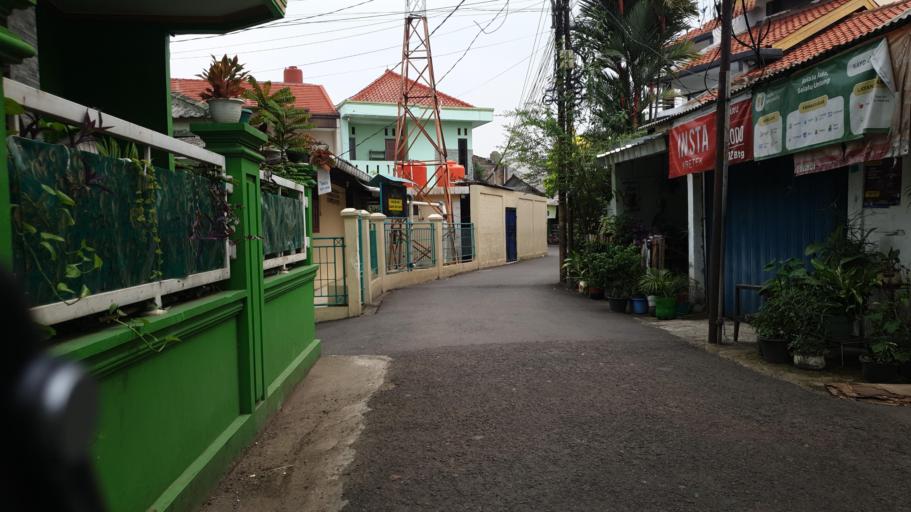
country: ID
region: West Java
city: Depok
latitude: -6.3307
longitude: 106.8246
